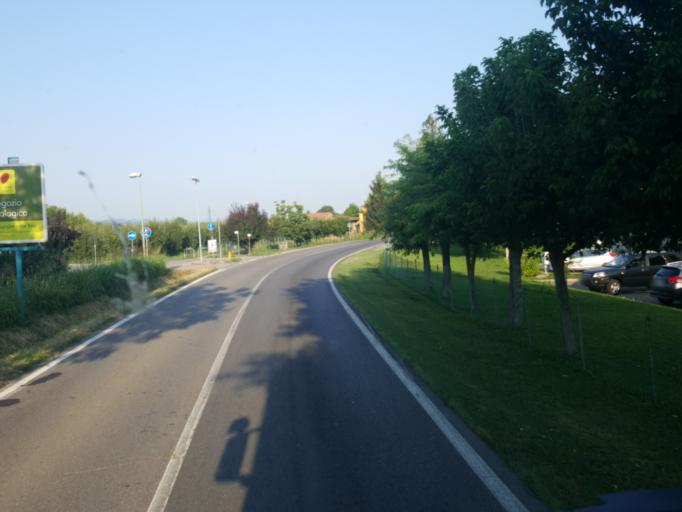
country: IT
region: Emilia-Romagna
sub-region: Provincia di Modena
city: Spilamberto
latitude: 44.5348
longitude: 11.0108
